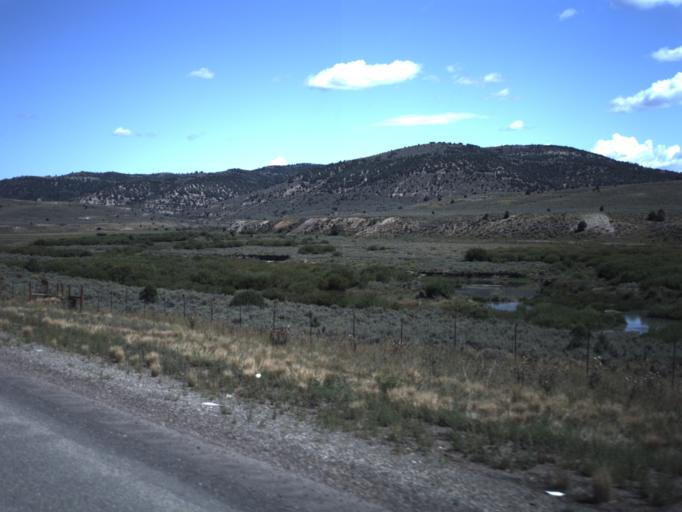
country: US
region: Utah
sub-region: Carbon County
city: Helper
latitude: 39.9104
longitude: -111.0613
